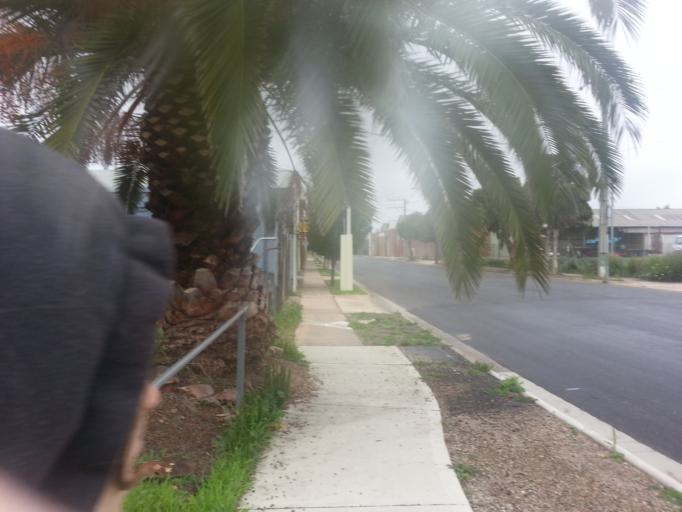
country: AU
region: South Australia
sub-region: Port Adelaide Enfield
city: Birkenhead
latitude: -34.8473
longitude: 138.5090
